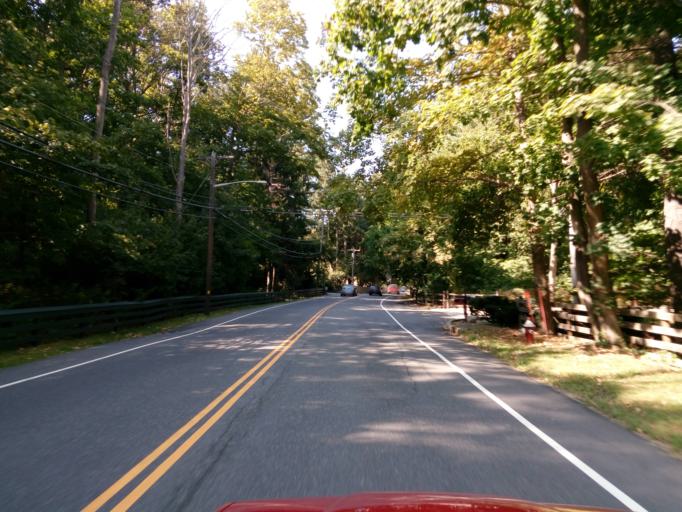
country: US
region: New York
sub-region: Nassau County
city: Upper Brookville
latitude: 40.8347
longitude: -73.5724
